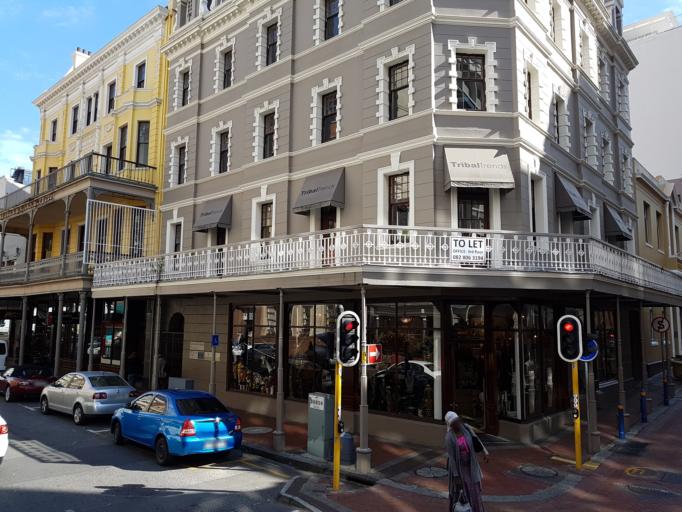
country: ZA
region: Western Cape
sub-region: City of Cape Town
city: Cape Town
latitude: -33.9220
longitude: 18.4197
